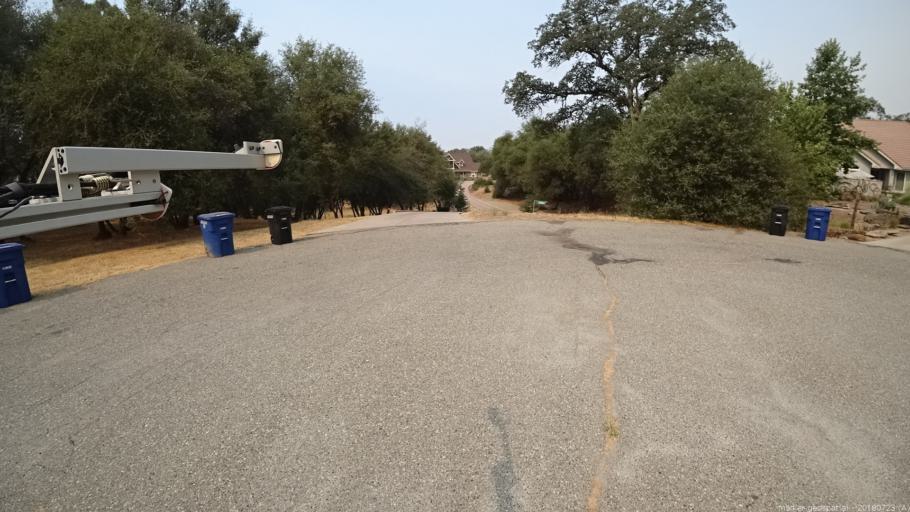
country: US
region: California
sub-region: Madera County
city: Ahwahnee
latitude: 37.3733
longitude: -119.7010
